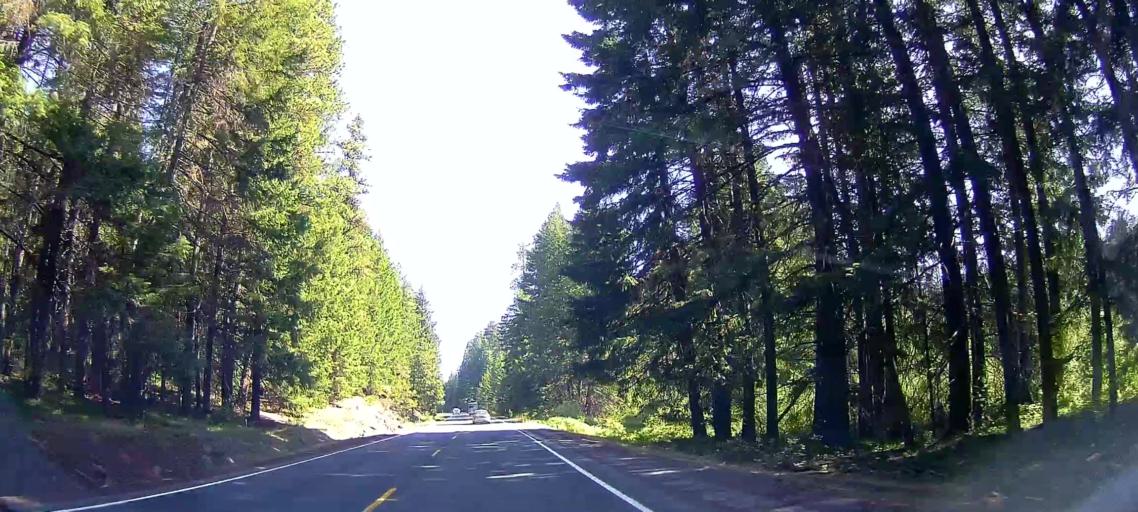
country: US
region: Oregon
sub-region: Jefferson County
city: Warm Springs
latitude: 45.0307
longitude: -121.5121
